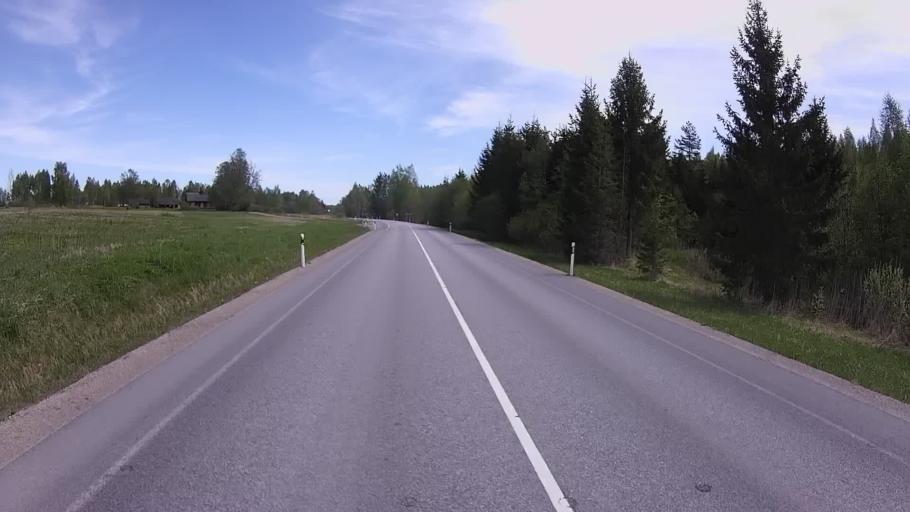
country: EE
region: Valgamaa
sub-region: Valga linn
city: Valga
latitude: 57.7128
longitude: 26.2158
